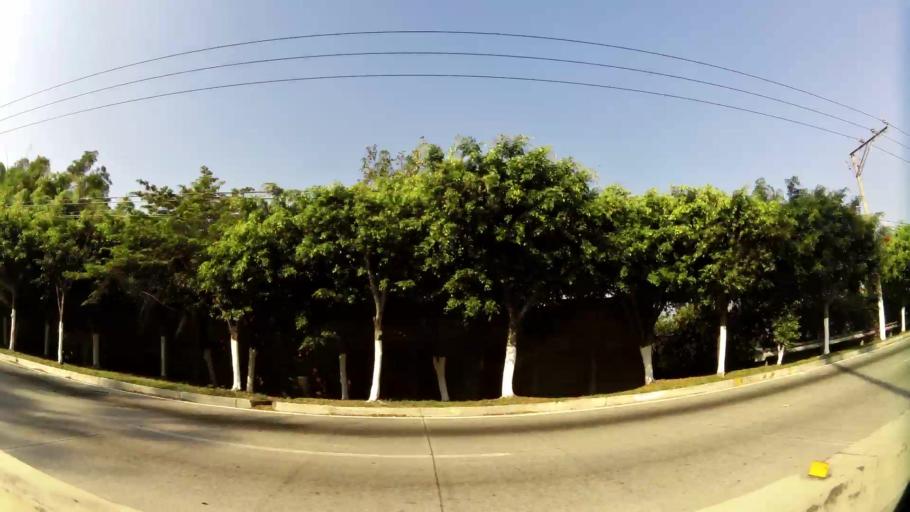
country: SV
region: San Salvador
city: San Salvador
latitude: 13.6758
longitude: -89.2190
